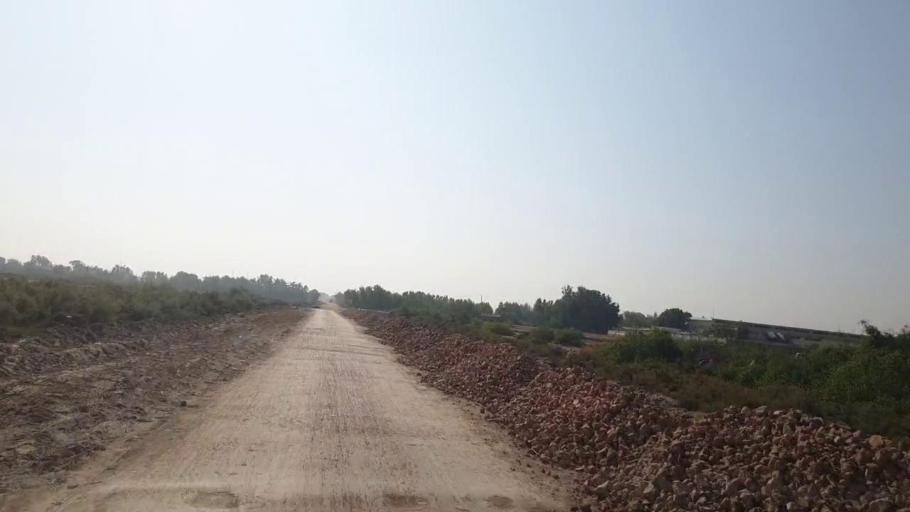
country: PK
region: Sindh
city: Thatta
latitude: 24.7665
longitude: 67.9134
